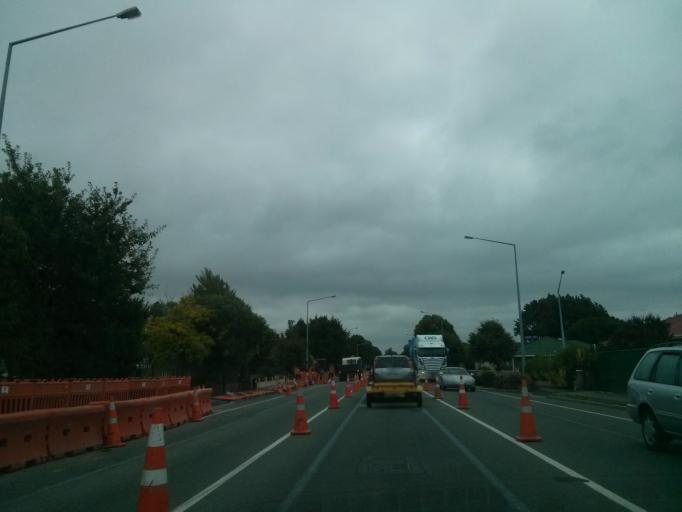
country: NZ
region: Canterbury
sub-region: Christchurch City
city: Christchurch
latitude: -43.5354
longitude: 172.5679
